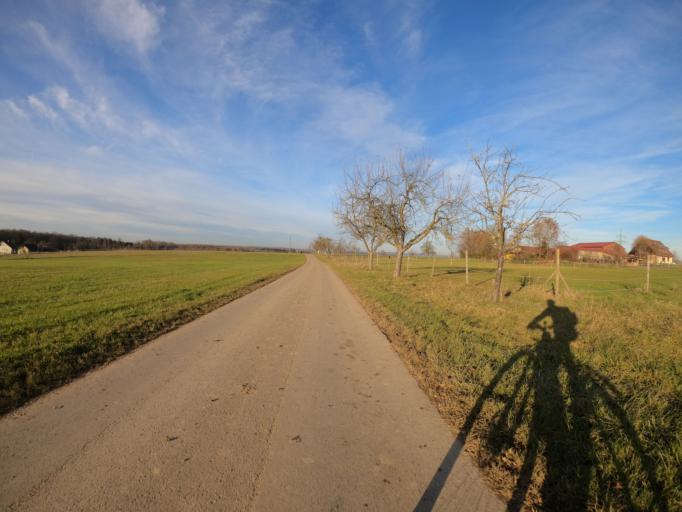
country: DE
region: Baden-Wuerttemberg
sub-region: Regierungsbezirk Stuttgart
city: Hattenhofen
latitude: 48.6674
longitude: 9.5533
